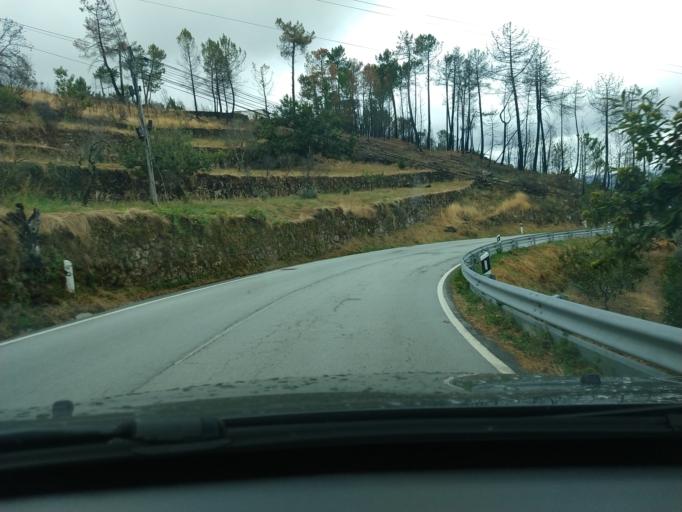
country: PT
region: Guarda
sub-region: Seia
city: Seia
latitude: 40.4165
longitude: -7.6855
